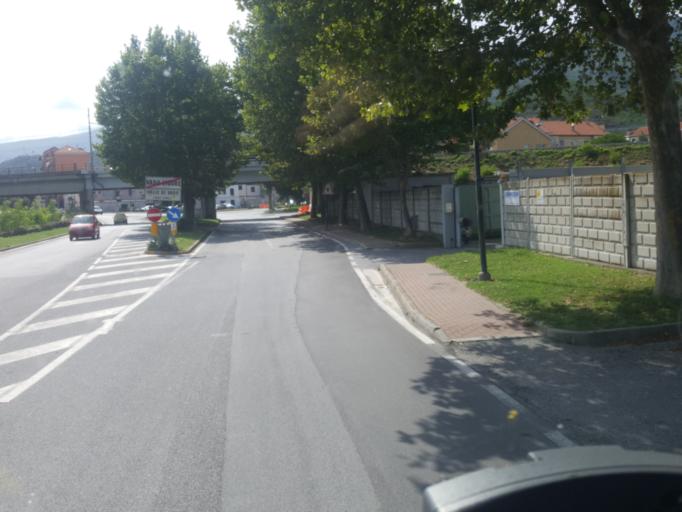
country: IT
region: Liguria
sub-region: Provincia di Savona
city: Valle di Vado
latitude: 44.2642
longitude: 8.4210
